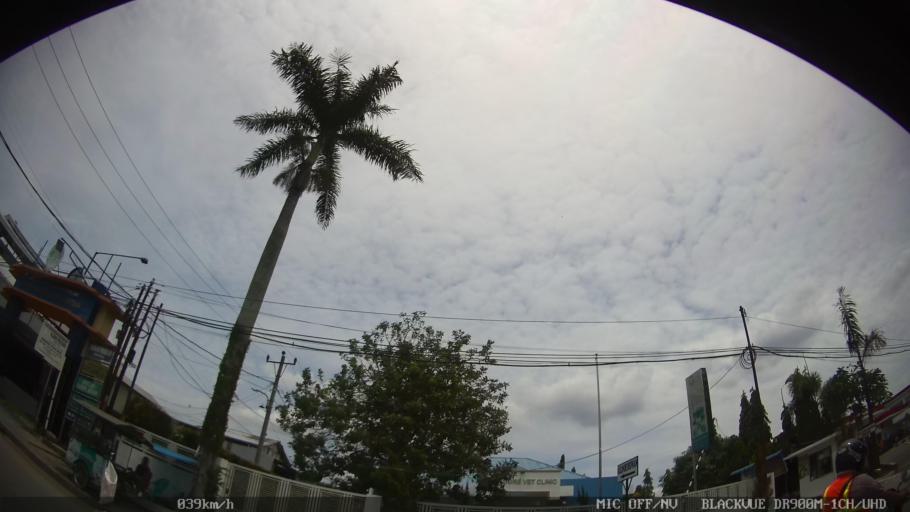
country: ID
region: North Sumatra
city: Deli Tua
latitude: 3.5315
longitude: 98.6430
